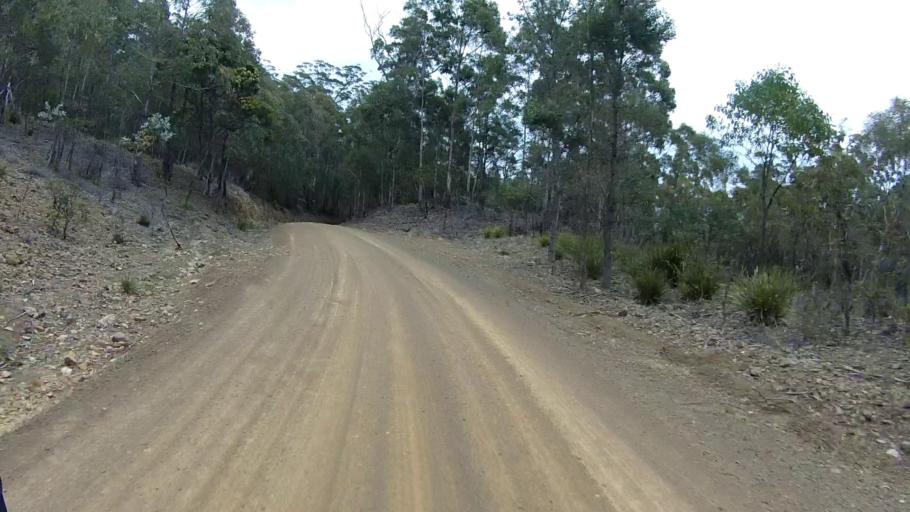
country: AU
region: Tasmania
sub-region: Sorell
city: Sorell
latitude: -42.6010
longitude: 147.8865
